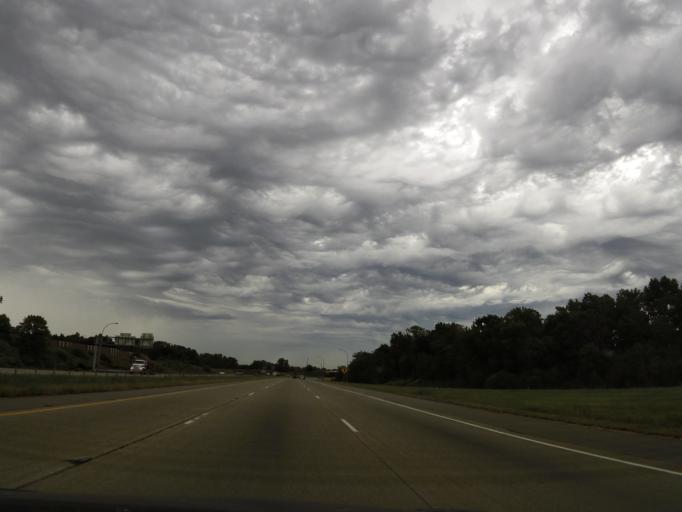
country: US
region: Minnesota
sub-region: Dakota County
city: Eagan
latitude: 44.8066
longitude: -93.1888
